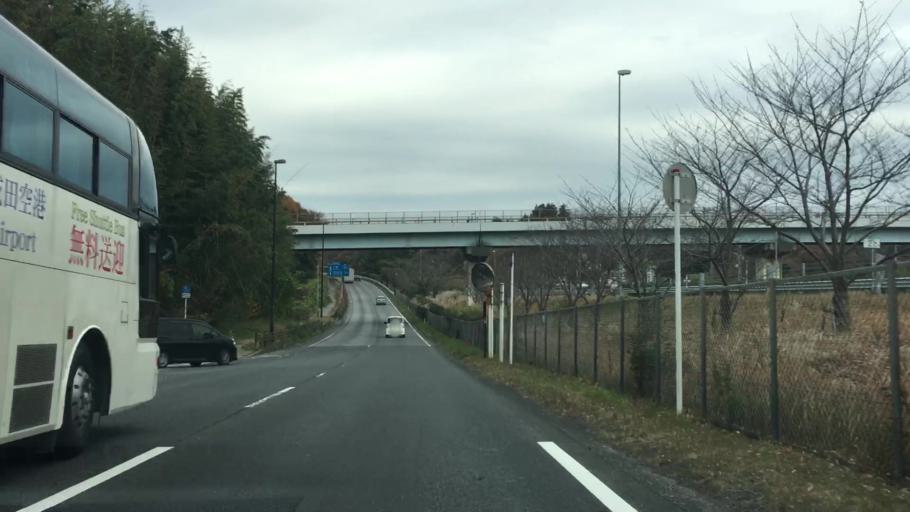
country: JP
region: Chiba
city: Narita
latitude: 35.7811
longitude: 140.3776
